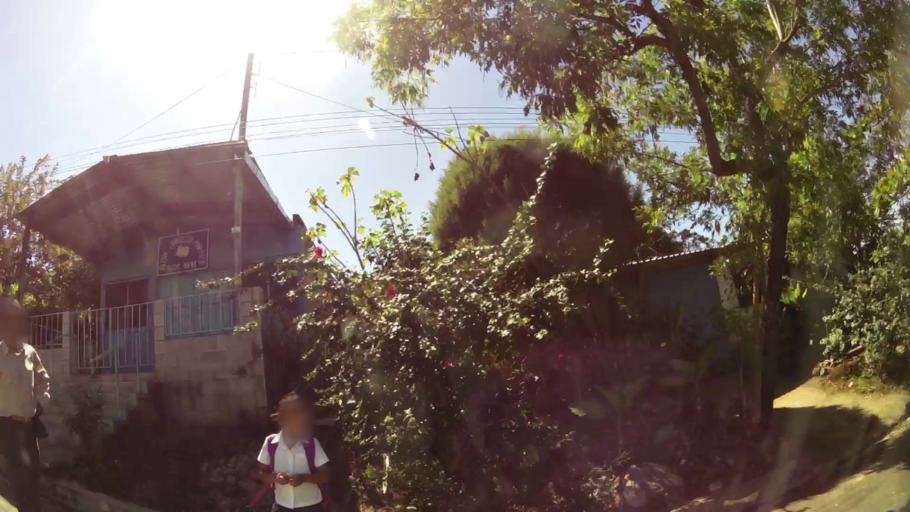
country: SV
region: Ahuachapan
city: Ahuachapan
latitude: 13.9342
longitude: -89.8391
